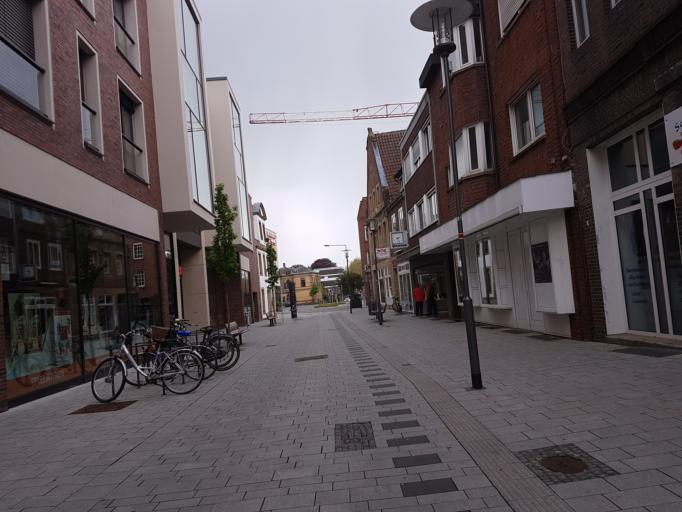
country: DE
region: North Rhine-Westphalia
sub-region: Regierungsbezirk Munster
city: Rheine
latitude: 52.2778
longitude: 7.4402
